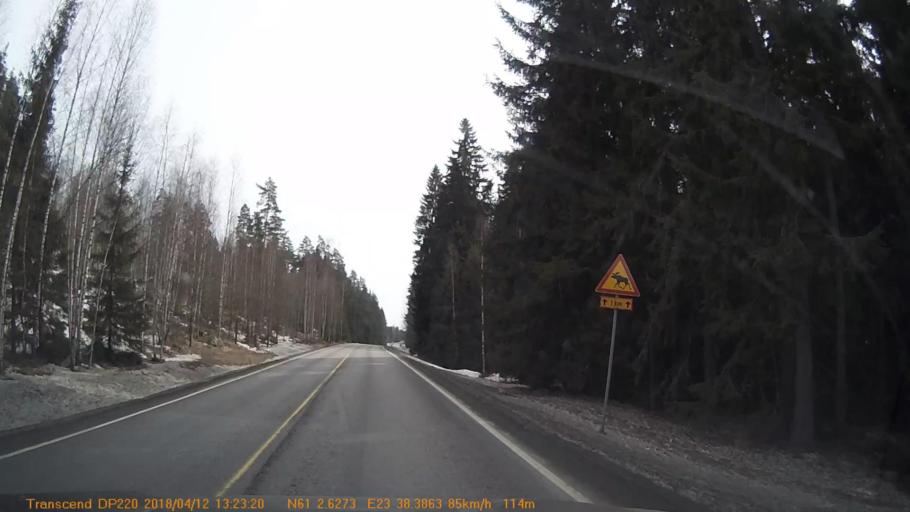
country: FI
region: Pirkanmaa
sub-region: Etelae-Pirkanmaa
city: Urjala
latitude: 61.0428
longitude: 23.6412
